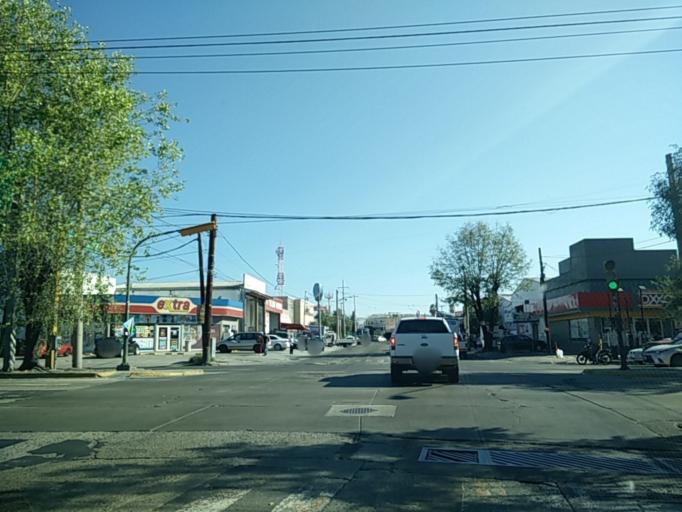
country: MX
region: Jalisco
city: Tlaquepaque
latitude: 20.6504
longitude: -103.3362
